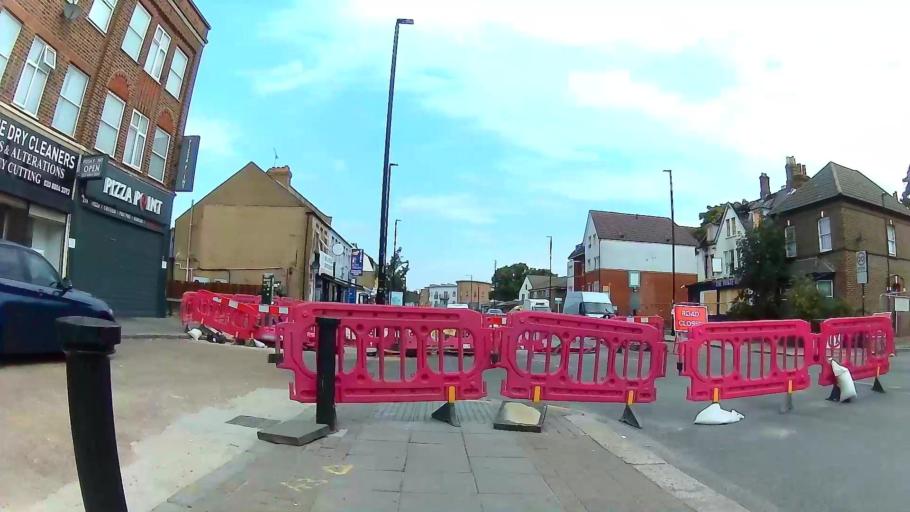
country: GB
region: England
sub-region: Greater London
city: Enfield
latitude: 51.6471
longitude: -0.0470
